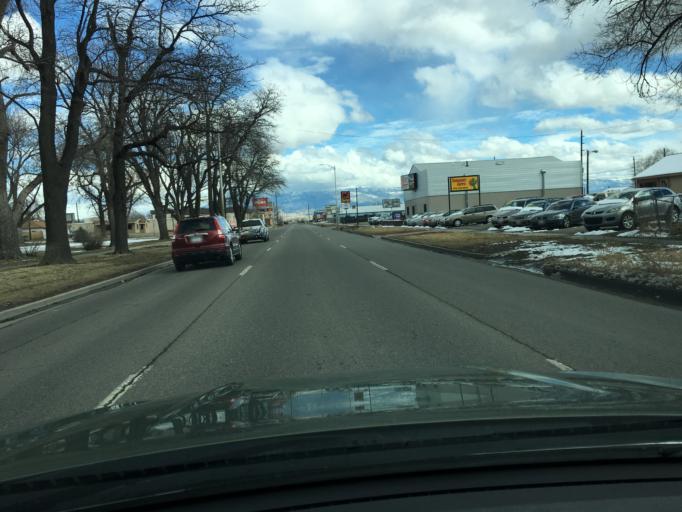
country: US
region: Colorado
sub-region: Mesa County
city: Grand Junction
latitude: 39.0644
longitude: -108.5573
